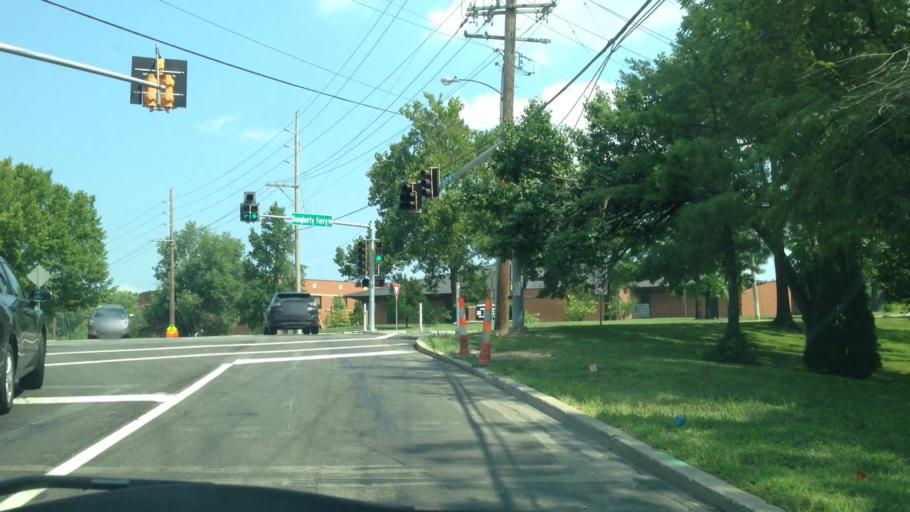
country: US
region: Missouri
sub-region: Saint Louis County
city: Des Peres
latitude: 38.5841
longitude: -90.4435
